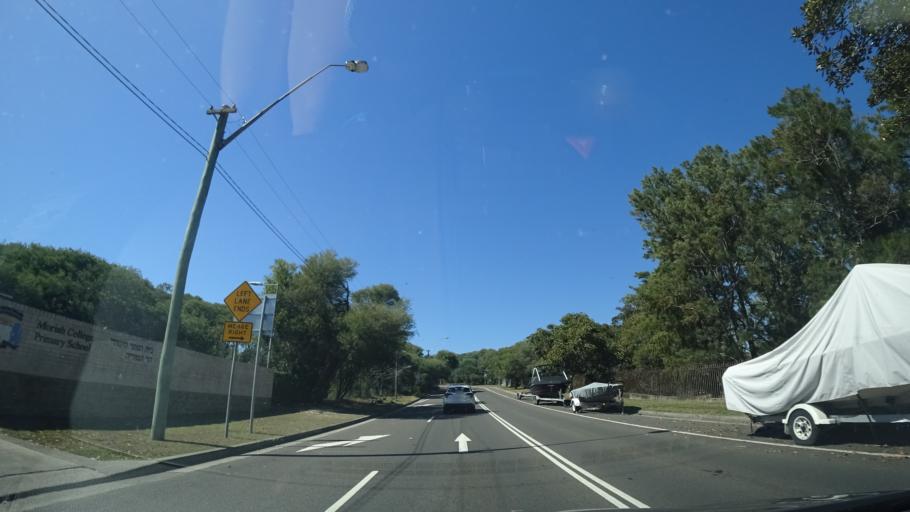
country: AU
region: New South Wales
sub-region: Waverley
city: Bondi Junction
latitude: -33.8992
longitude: 151.2422
